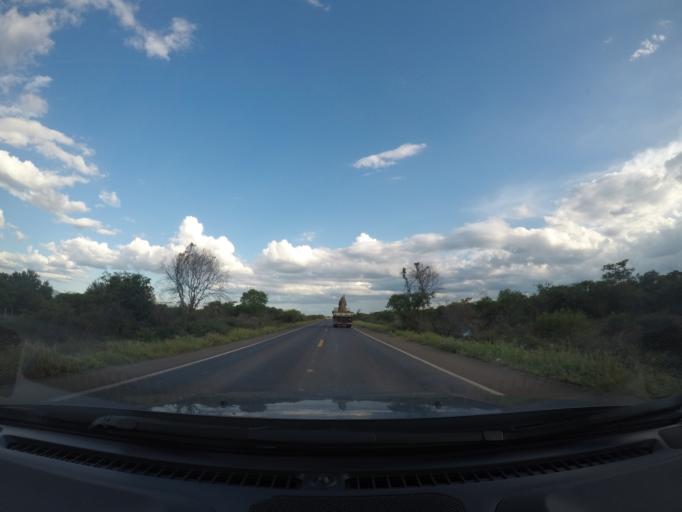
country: BR
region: Bahia
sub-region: Oliveira Dos Brejinhos
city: Beira Rio
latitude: -12.2087
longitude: -42.8046
